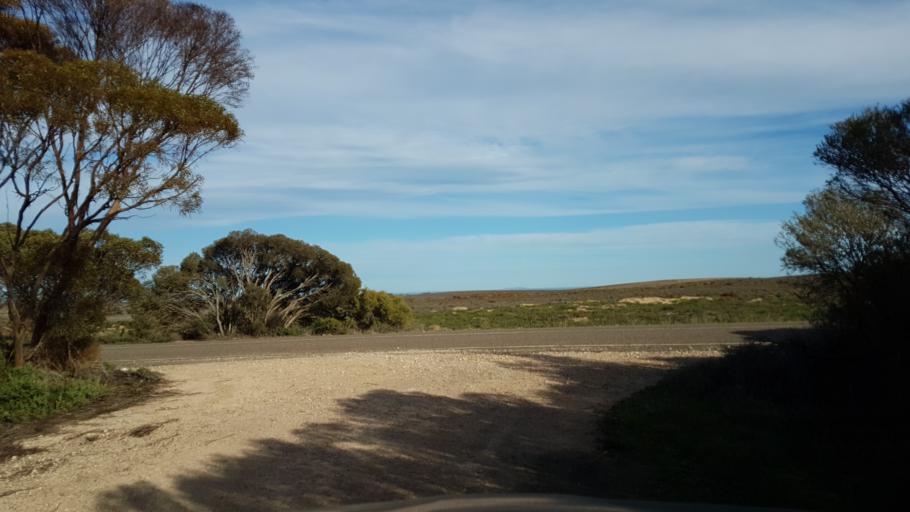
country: AU
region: South Australia
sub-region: Murray Bridge
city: Tailem Bend
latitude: -35.0634
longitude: 139.4657
